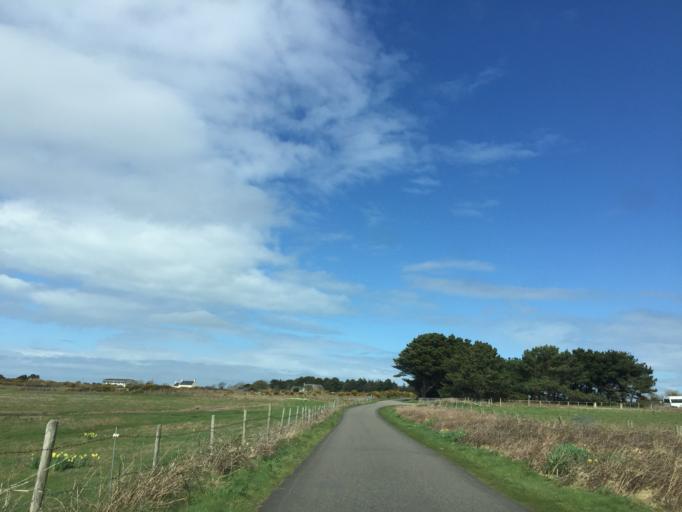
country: JE
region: St Helier
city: Saint Helier
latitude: 49.1699
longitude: -2.1694
